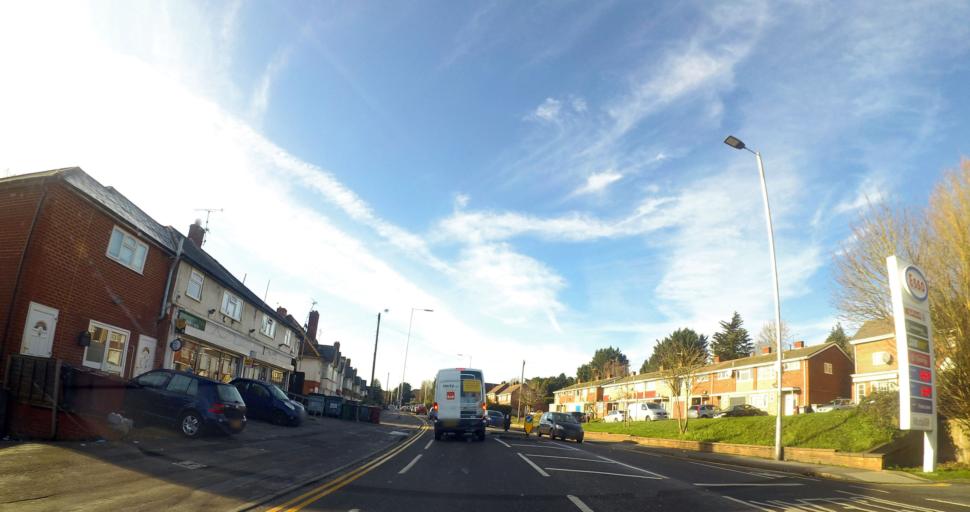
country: GB
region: England
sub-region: Reading
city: Reading
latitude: 51.4479
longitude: -0.9805
